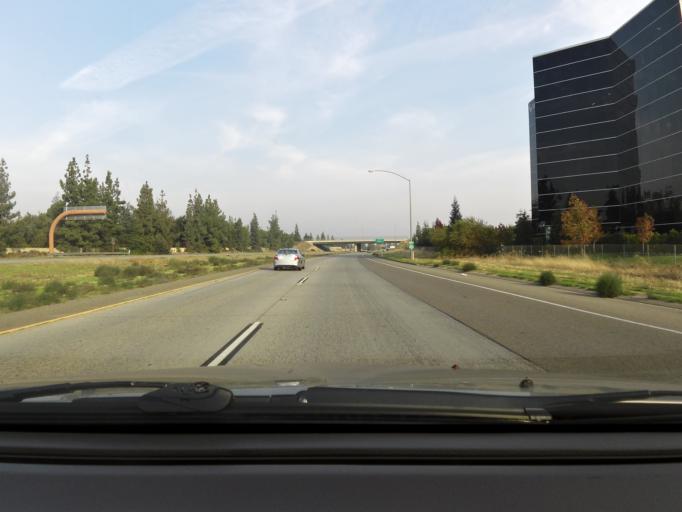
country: US
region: California
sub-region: Fresno County
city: Clovis
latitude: 36.8580
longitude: -119.7907
